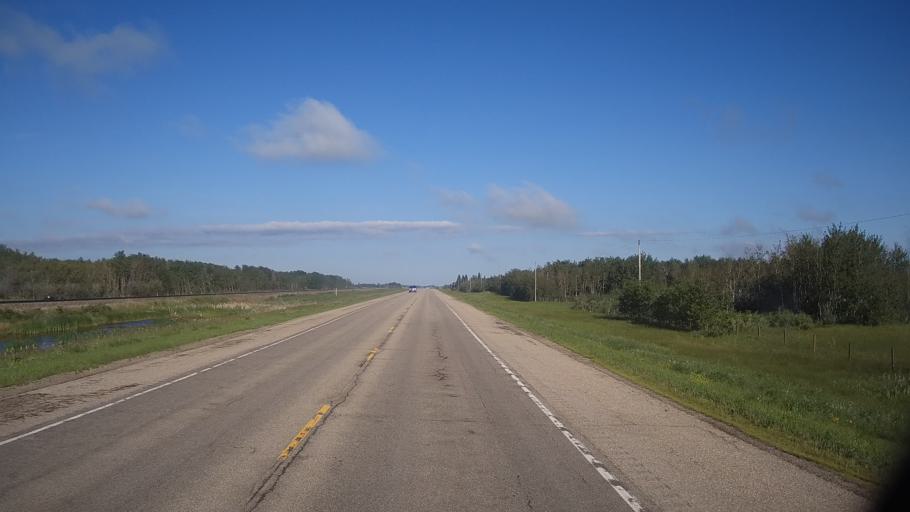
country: CA
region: Saskatchewan
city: Lanigan
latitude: 51.8555
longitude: -105.0883
